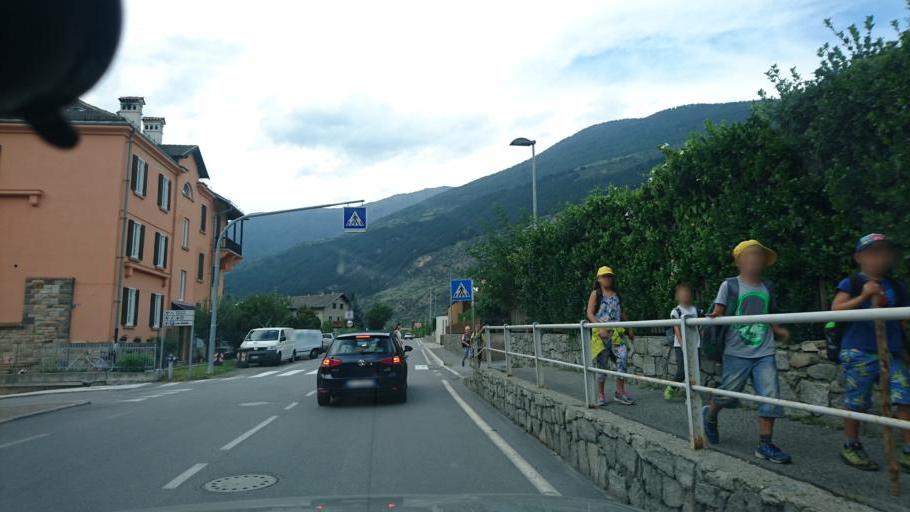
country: IT
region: Trentino-Alto Adige
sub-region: Bolzano
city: Lasa
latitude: 46.6184
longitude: 10.6964
